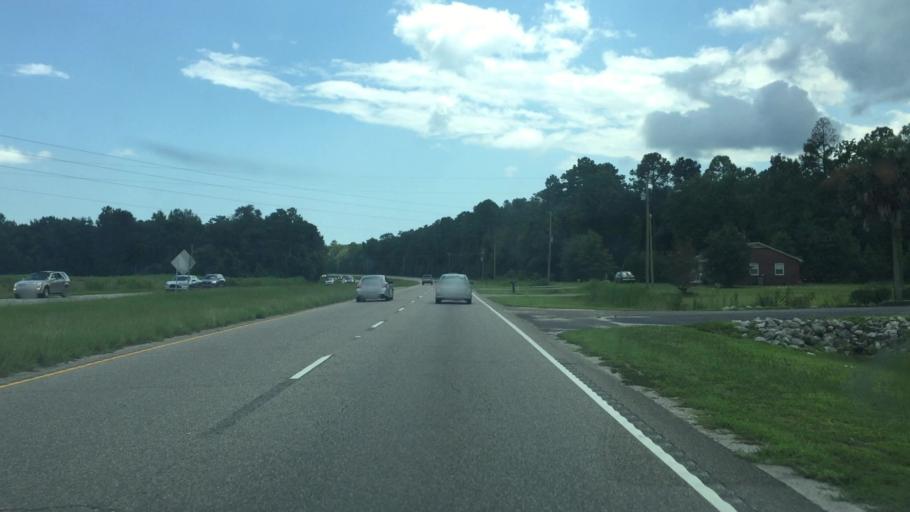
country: US
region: South Carolina
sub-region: Horry County
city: North Myrtle Beach
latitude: 33.9243
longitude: -78.7261
